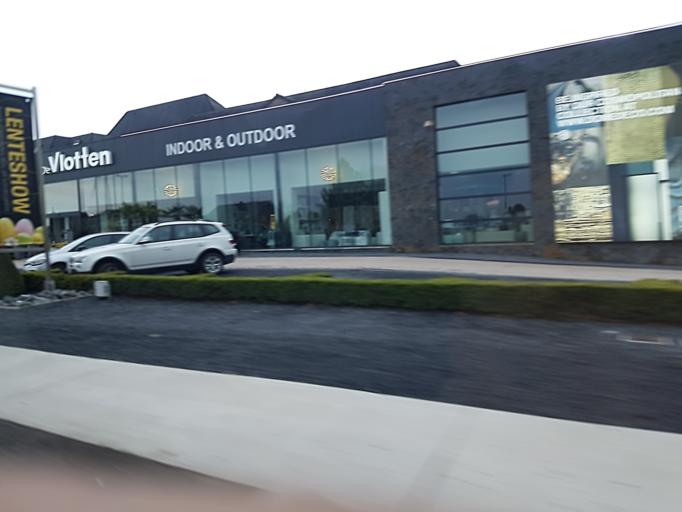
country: BE
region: Flanders
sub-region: Provincie Limburg
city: Maasmechelen
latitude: 50.9482
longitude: 5.6932
